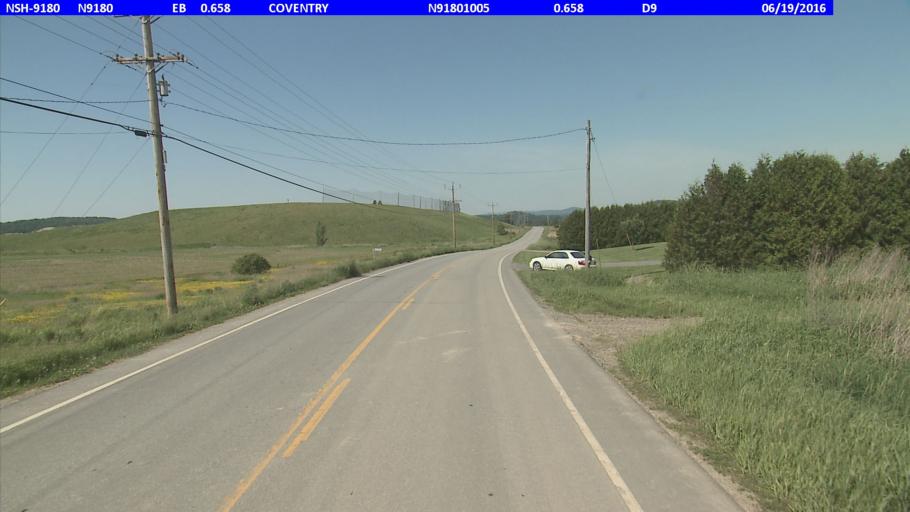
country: US
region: Vermont
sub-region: Orleans County
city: Newport
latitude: 44.8983
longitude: -72.2252
